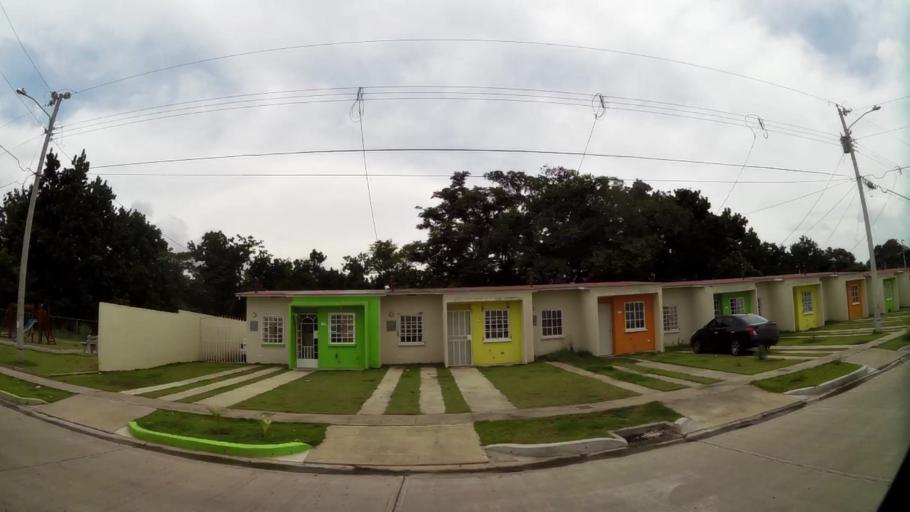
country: PA
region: Panama
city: Cabra Numero Uno
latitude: 9.1222
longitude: -79.3217
